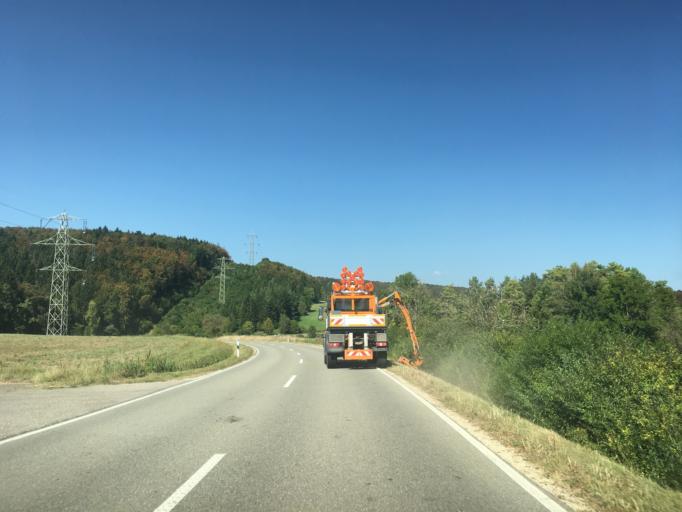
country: DE
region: Baden-Wuerttemberg
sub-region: Tuebingen Region
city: Hayingen
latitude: 48.2879
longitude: 9.4799
